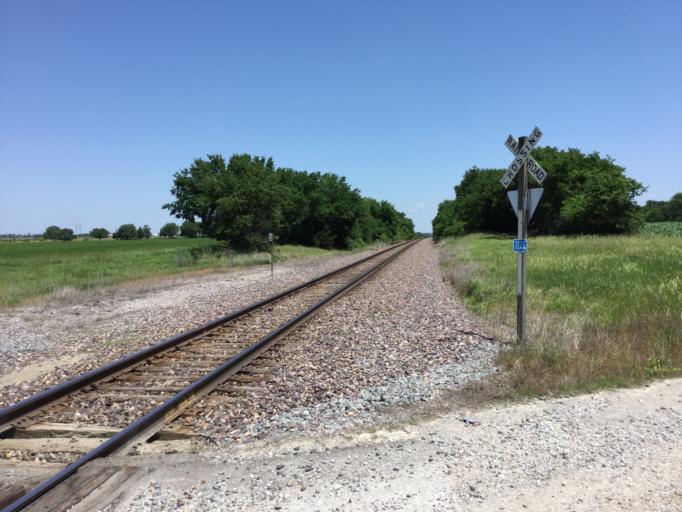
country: US
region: Kansas
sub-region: Anderson County
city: Garnett
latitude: 38.1683
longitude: -95.0617
